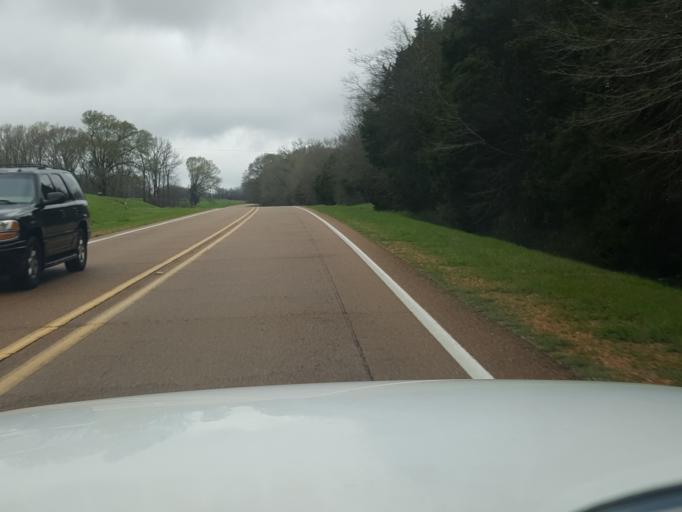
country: US
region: Mississippi
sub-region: Madison County
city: Canton
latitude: 32.7683
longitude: -90.1746
